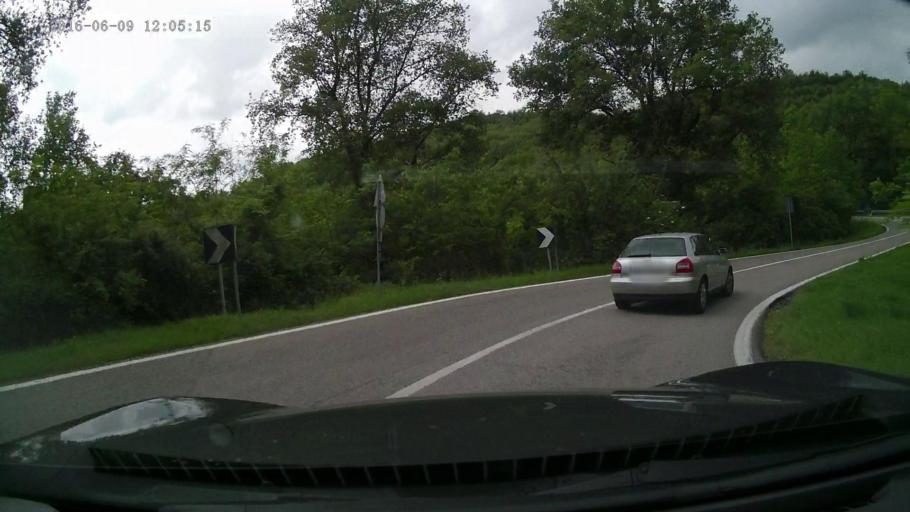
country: IT
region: Tuscany
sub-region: Province of Florence
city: Panzano in Chianti
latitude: 43.5200
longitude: 11.2937
